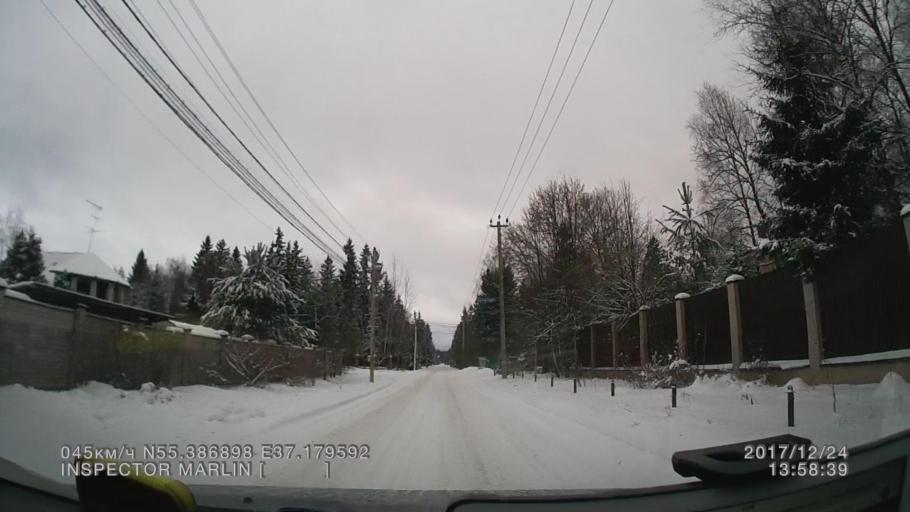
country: RU
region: Moskovskaya
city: Troitsk
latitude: 55.3868
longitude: 37.1795
